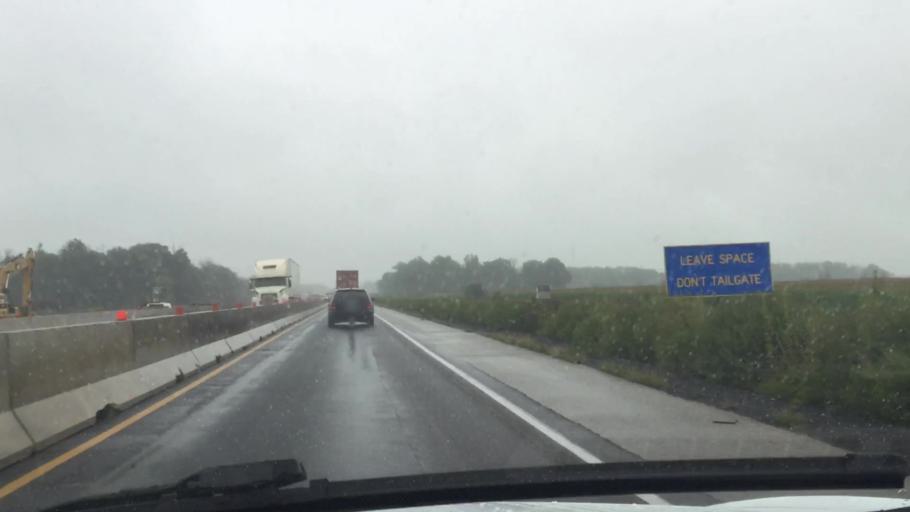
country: CA
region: Ontario
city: Delaware
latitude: 42.7877
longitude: -81.3574
